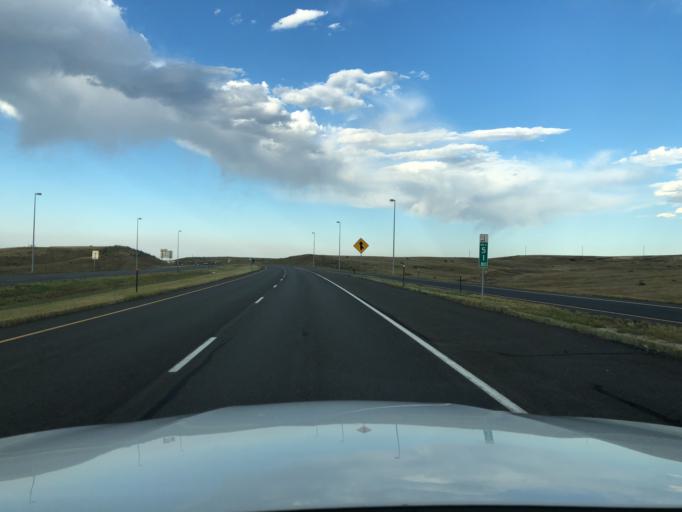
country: US
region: Colorado
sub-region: Boulder County
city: Lafayette
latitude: 39.9604
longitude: -105.0811
